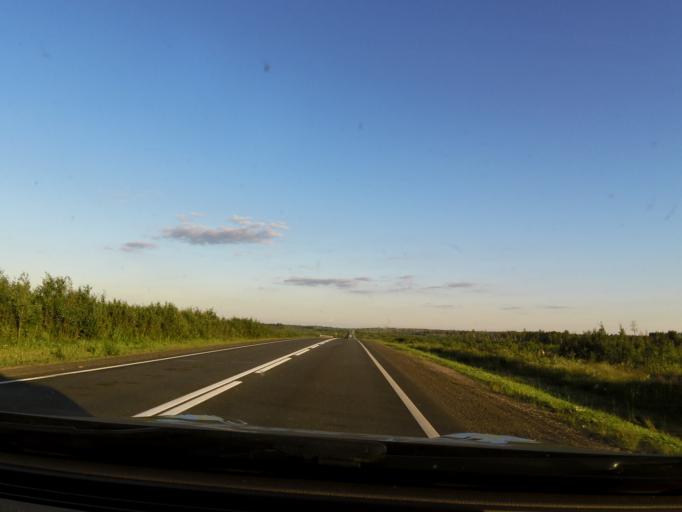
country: RU
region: Jaroslavl
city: Prechistoye
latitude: 58.6217
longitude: 40.3320
